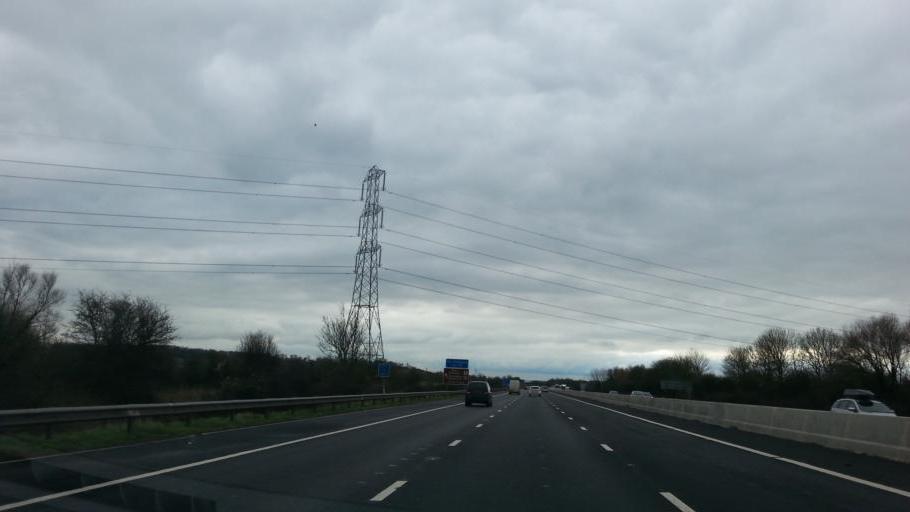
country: GB
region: England
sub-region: Somerset
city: Puriton
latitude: 51.1823
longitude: -2.9753
